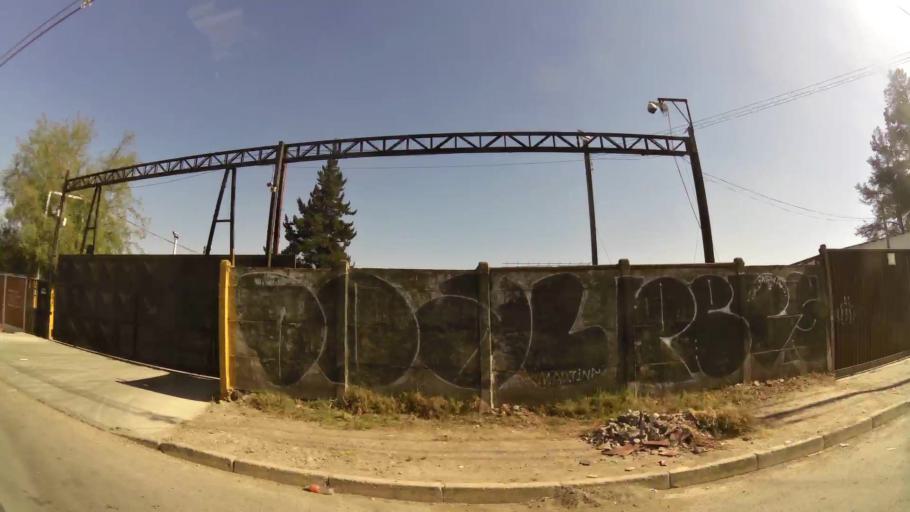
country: CL
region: Santiago Metropolitan
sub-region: Provincia de Maipo
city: San Bernardo
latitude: -33.5702
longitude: -70.7064
